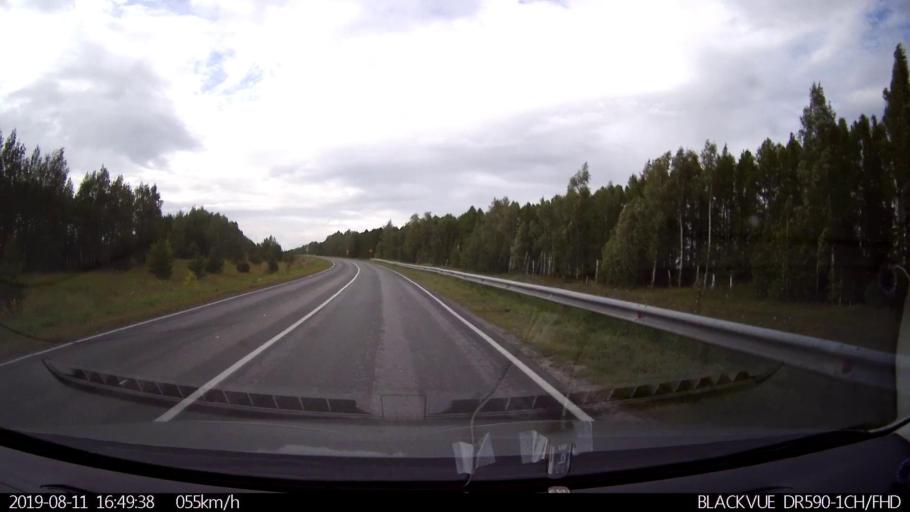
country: RU
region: Ulyanovsk
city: Mayna
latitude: 54.2223
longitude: 47.6957
